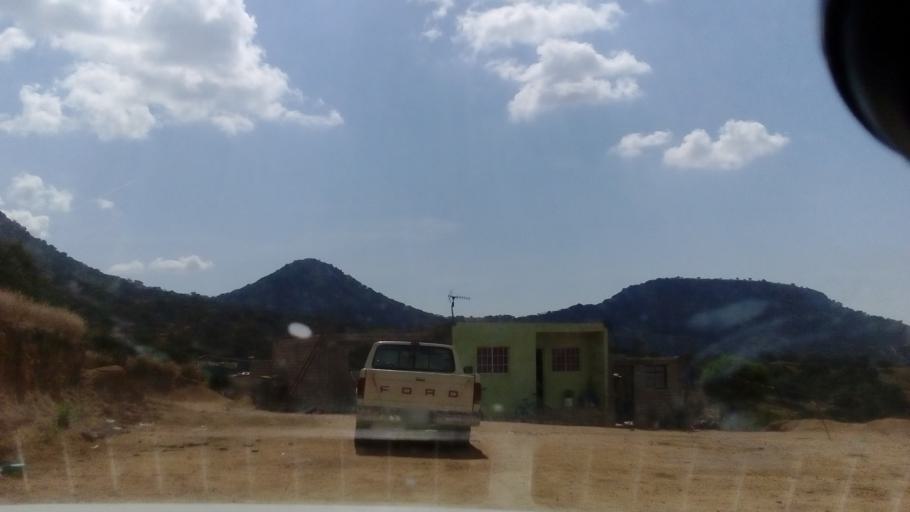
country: MX
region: Guanajuato
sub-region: Silao de la Victoria
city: San Francisco (Banos de Agua Caliente)
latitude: 21.1581
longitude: -101.4626
